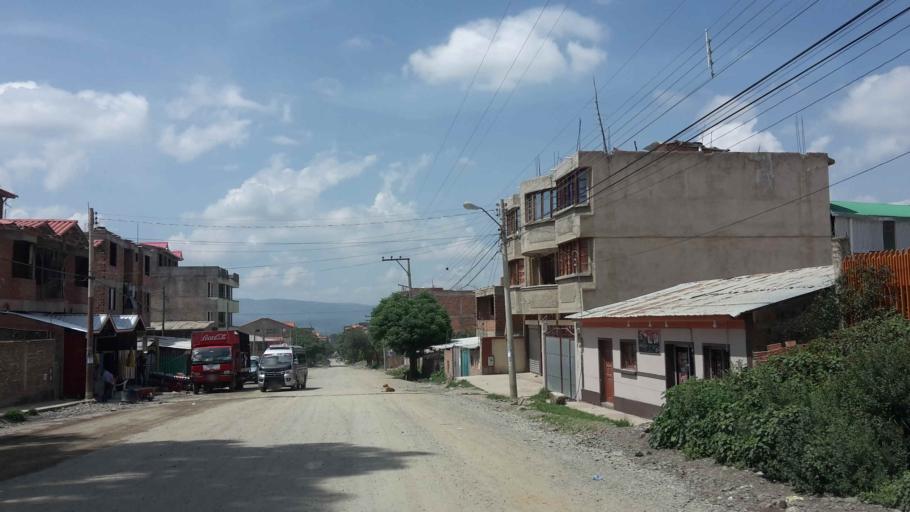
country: BO
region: Cochabamba
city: Cochabamba
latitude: -17.3310
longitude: -66.2189
